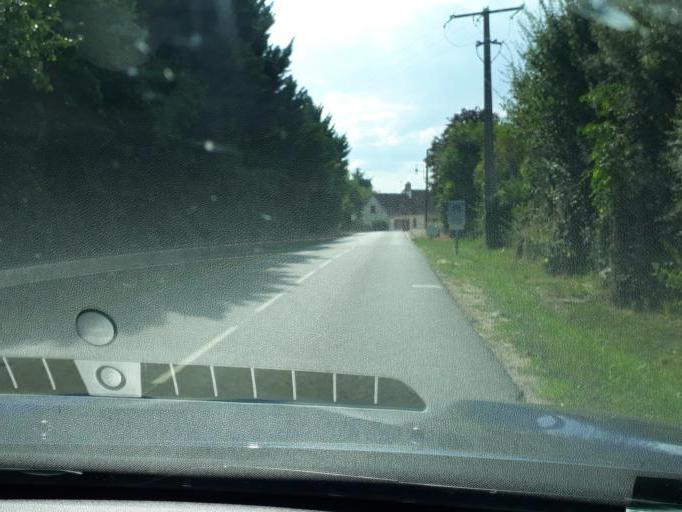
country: FR
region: Centre
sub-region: Departement du Cher
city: Nerondes
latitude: 47.0483
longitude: 2.8743
